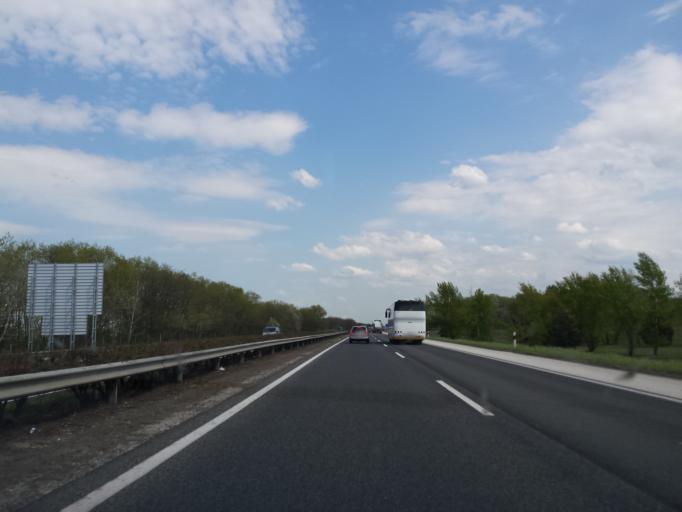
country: HU
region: Gyor-Moson-Sopron
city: Bony
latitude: 47.6845
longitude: 17.8679
